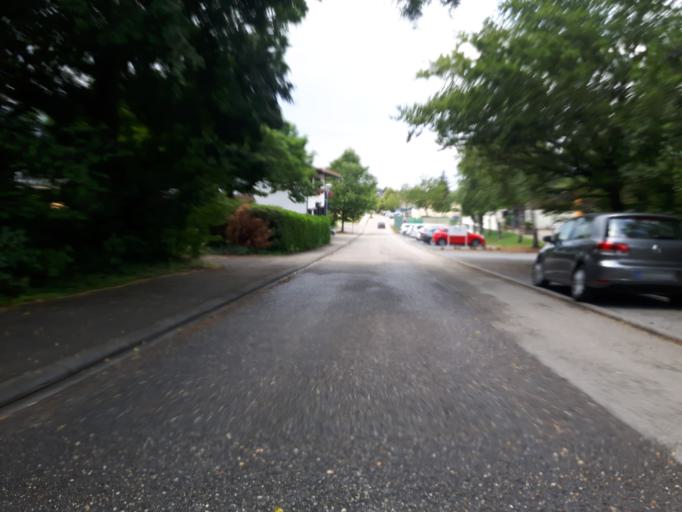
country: DE
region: Baden-Wuerttemberg
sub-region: Regierungsbezirk Stuttgart
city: Eppingen
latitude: 49.1312
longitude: 8.9301
